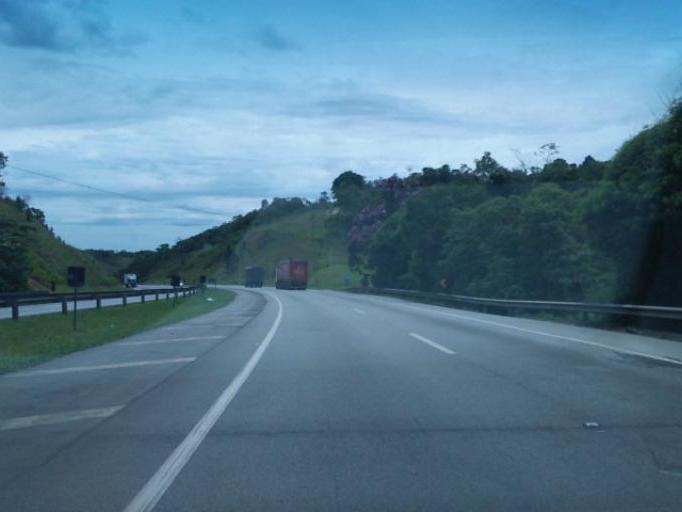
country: BR
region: Sao Paulo
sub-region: Juquitiba
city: Juquitiba
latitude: -23.9879
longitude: -47.1486
